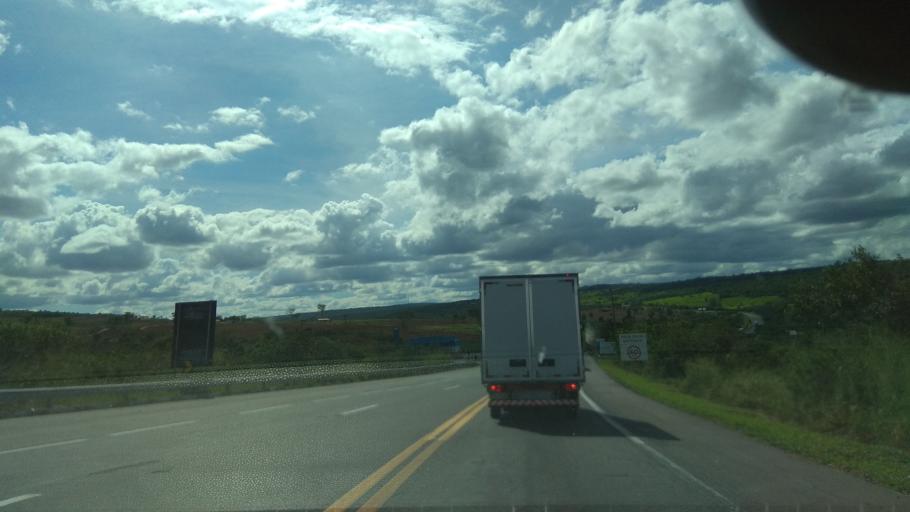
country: BR
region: Bahia
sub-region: Santa Ines
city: Santa Ines
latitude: -13.1642
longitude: -39.9992
